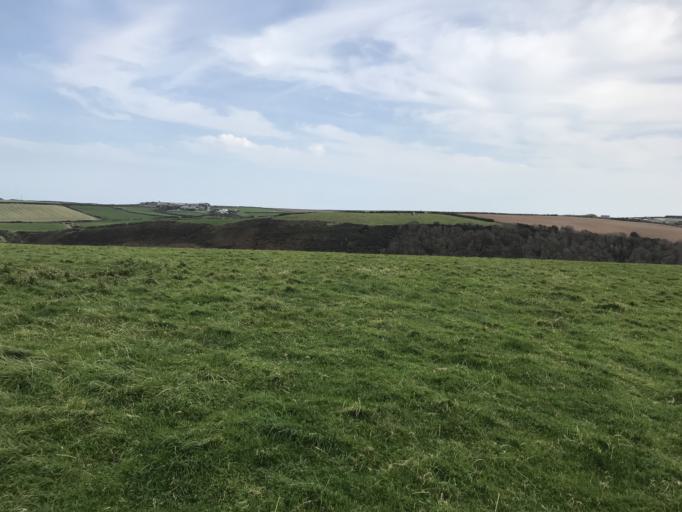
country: GB
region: England
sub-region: Cornwall
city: Flexbury
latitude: 50.9977
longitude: -4.5288
